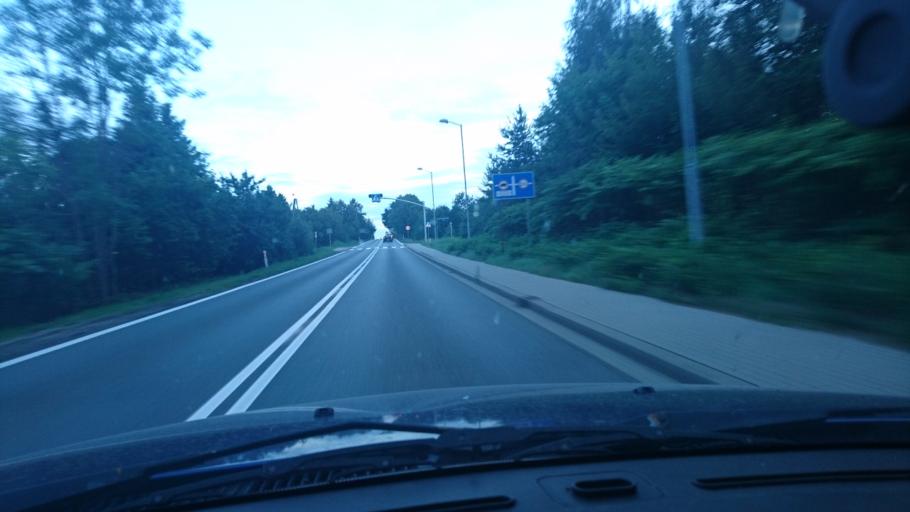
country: PL
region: Silesian Voivodeship
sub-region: Powiat tarnogorski
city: Tarnowskie Gory
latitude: 50.4468
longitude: 18.8366
